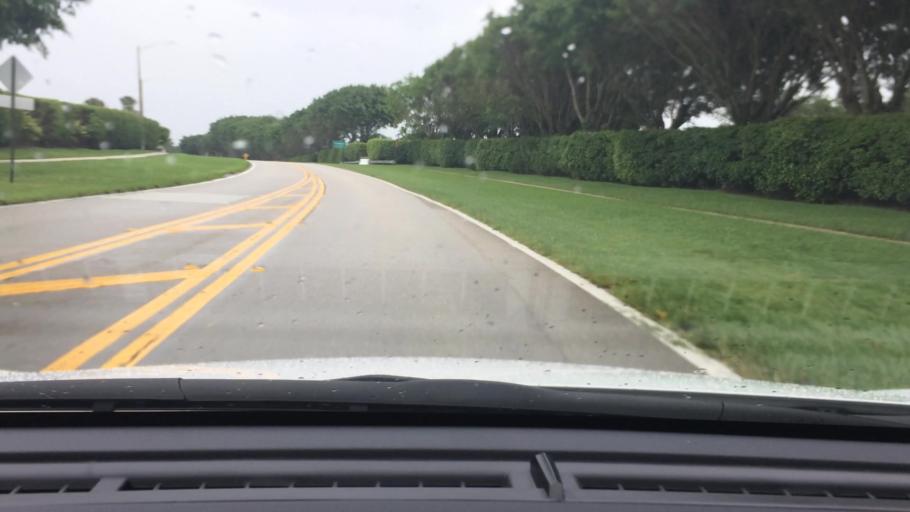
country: US
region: Florida
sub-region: Palm Beach County
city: Seminole Manor
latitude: 26.5497
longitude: -80.1647
